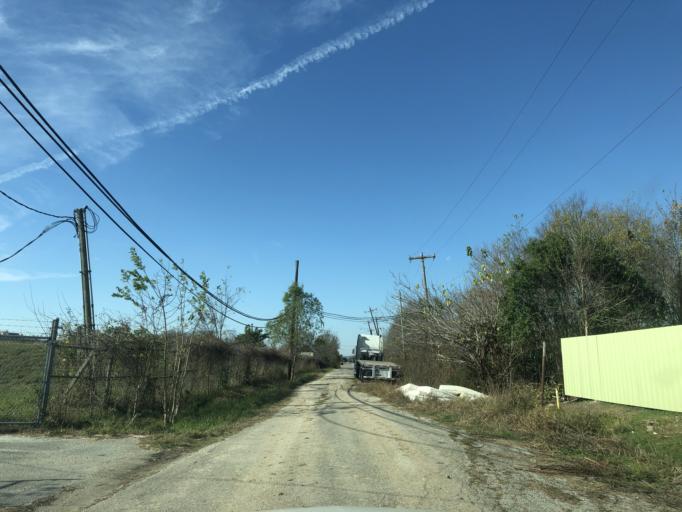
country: US
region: Texas
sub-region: Harris County
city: South Houston
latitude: 29.6613
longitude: -95.2498
